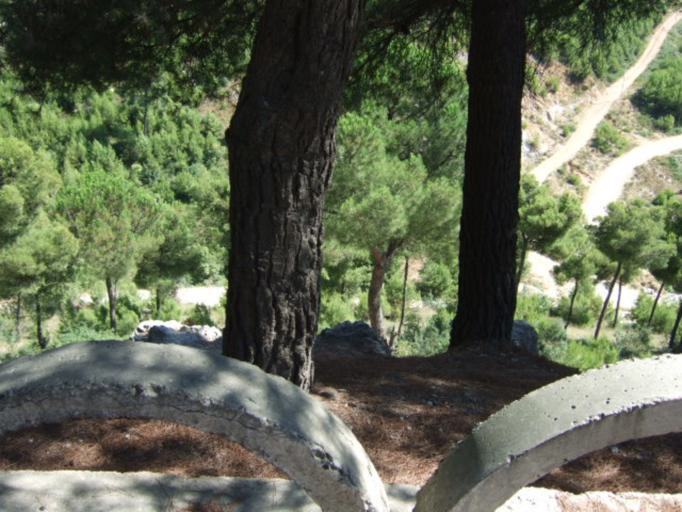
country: AL
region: Durres
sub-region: Rrethi i Krujes
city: Kruje
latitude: 41.4930
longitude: 19.7719
